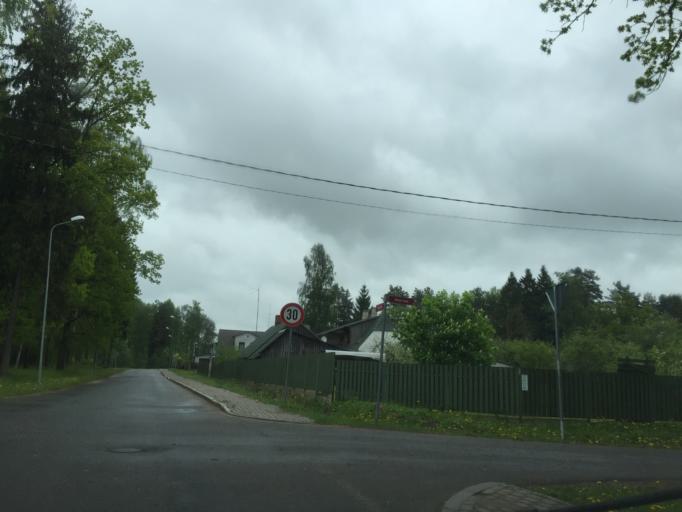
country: LV
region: Lielvarde
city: Lielvarde
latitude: 56.7286
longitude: 24.8085
